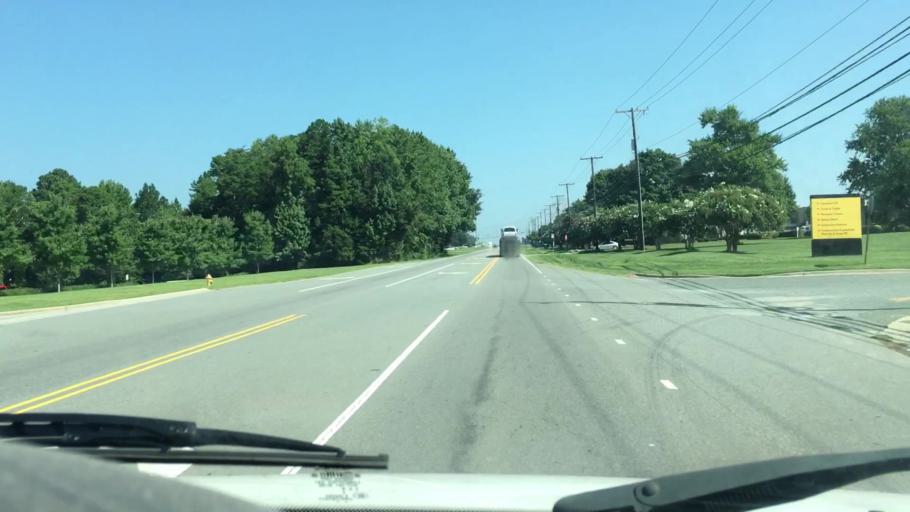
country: US
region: North Carolina
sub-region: Mecklenburg County
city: Huntersville
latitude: 35.3414
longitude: -80.8420
